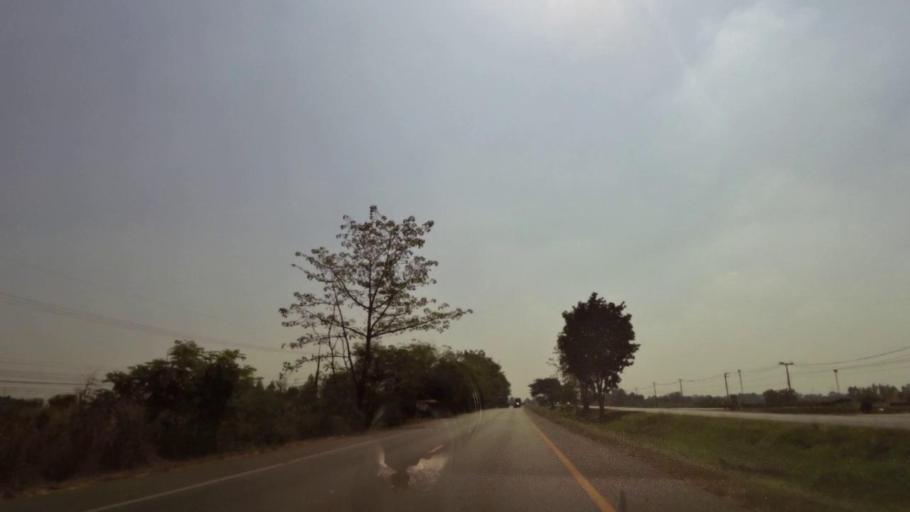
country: TH
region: Phichit
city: Wachira Barami
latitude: 16.4818
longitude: 100.1470
